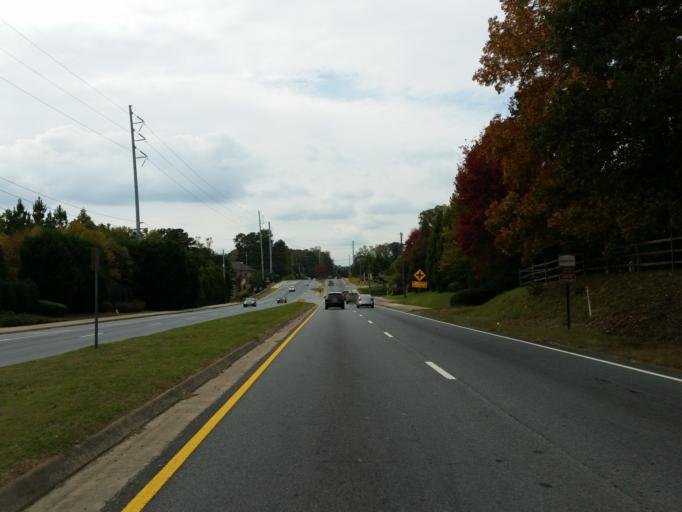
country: US
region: Georgia
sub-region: Cobb County
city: Marietta
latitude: 33.9777
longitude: -84.4665
